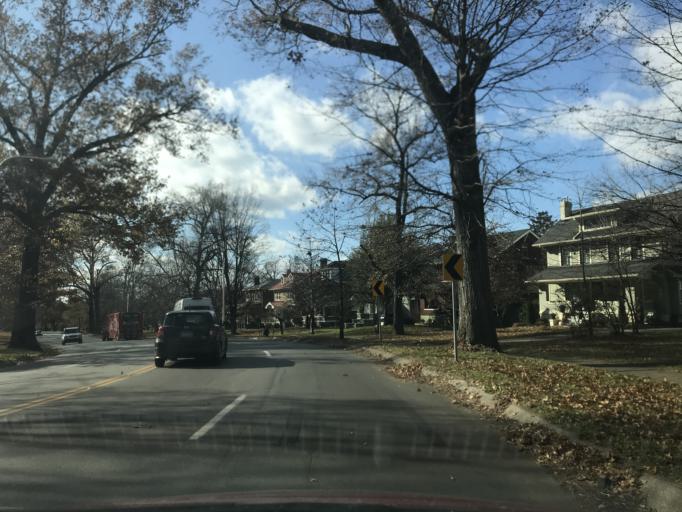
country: US
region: Kentucky
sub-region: Jefferson County
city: Audubon Park
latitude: 38.2265
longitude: -85.7210
